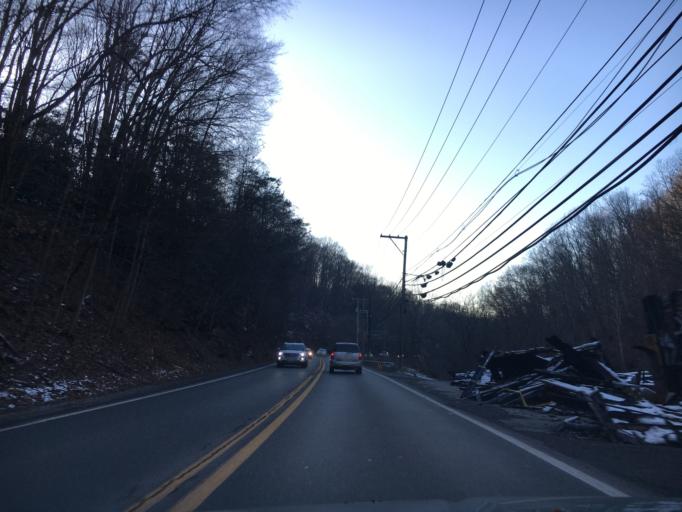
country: US
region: West Virginia
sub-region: Raleigh County
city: Beaver
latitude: 37.7557
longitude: -81.1521
